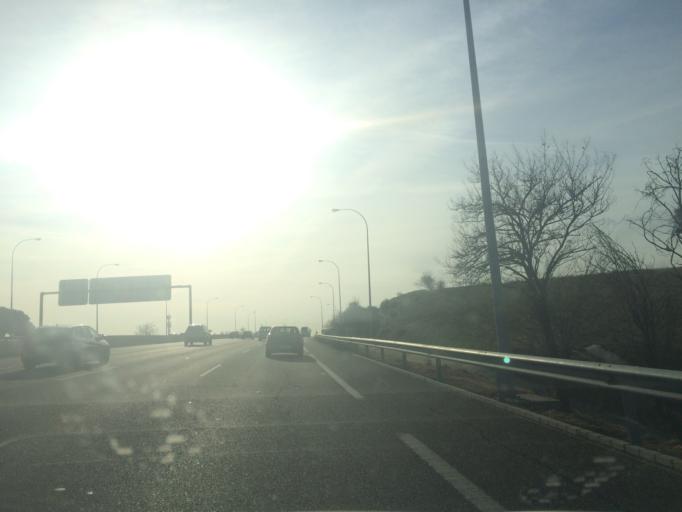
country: ES
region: Madrid
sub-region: Provincia de Madrid
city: Fuencarral-El Pardo
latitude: 40.4989
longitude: -3.7234
